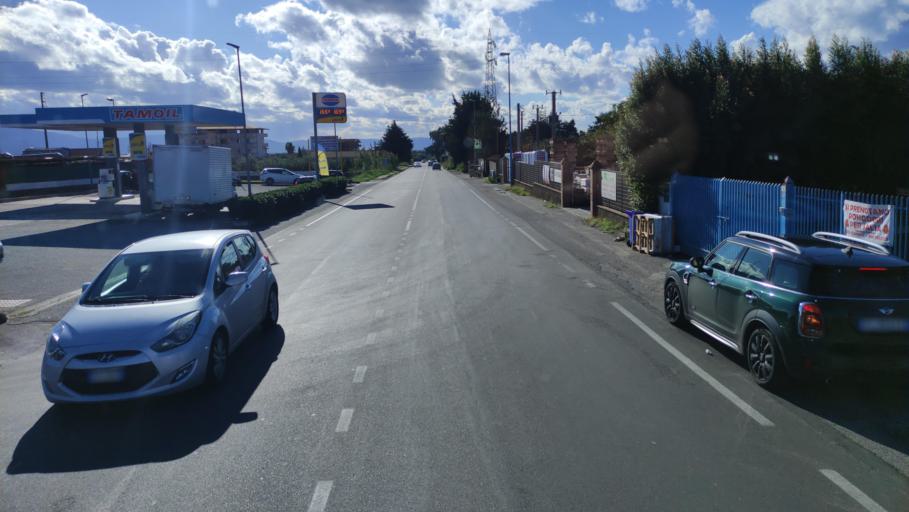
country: IT
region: Calabria
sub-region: Provincia di Catanzaro
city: Nicastro-Sambiase
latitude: 38.9334
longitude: 16.2877
